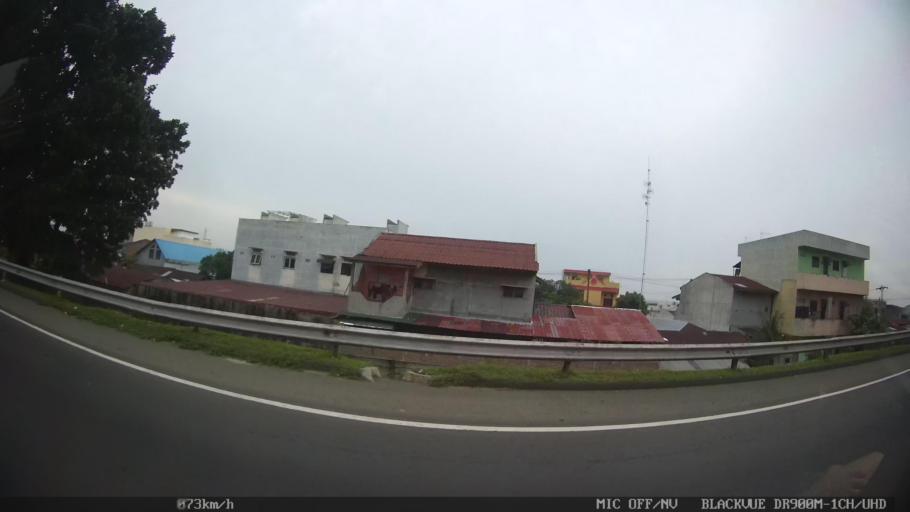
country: ID
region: North Sumatra
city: Medan
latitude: 3.5773
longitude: 98.7250
